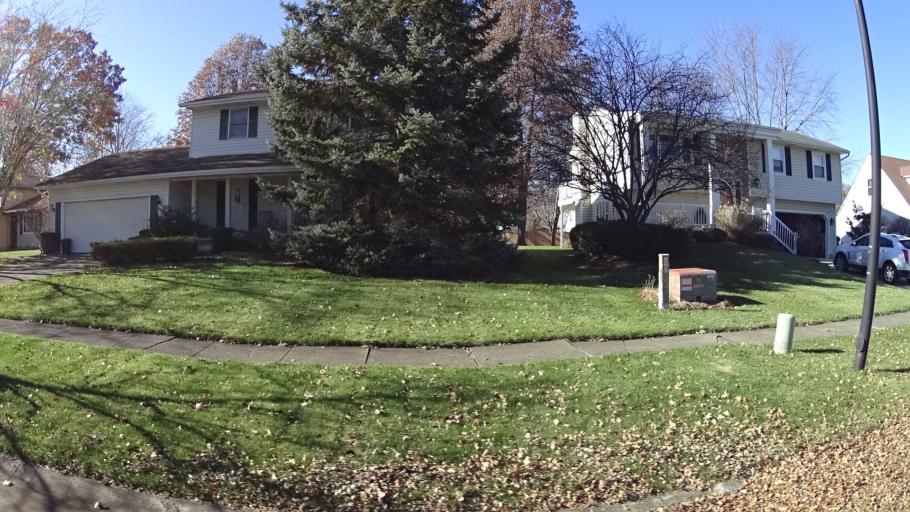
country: US
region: Ohio
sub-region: Lorain County
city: Elyria
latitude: 41.3447
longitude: -82.0738
